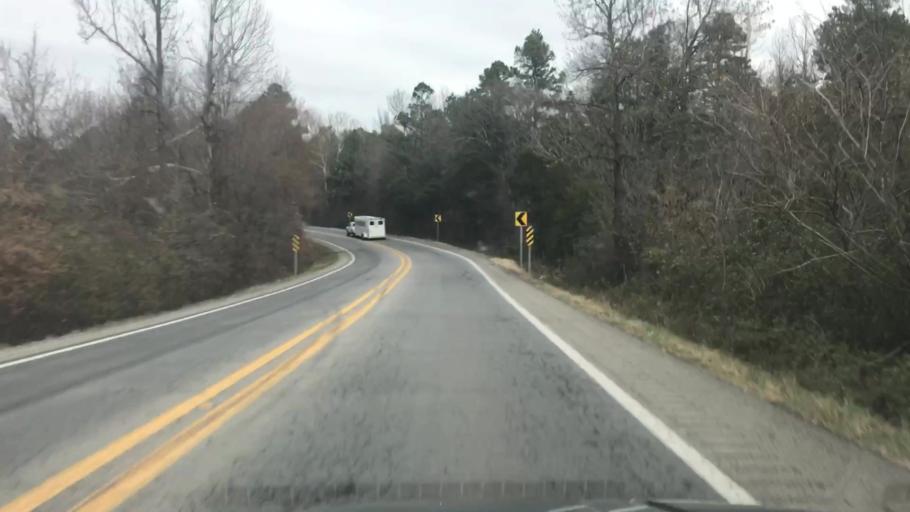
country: US
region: Arkansas
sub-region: Scott County
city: Waldron
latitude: 34.9508
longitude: -94.1052
